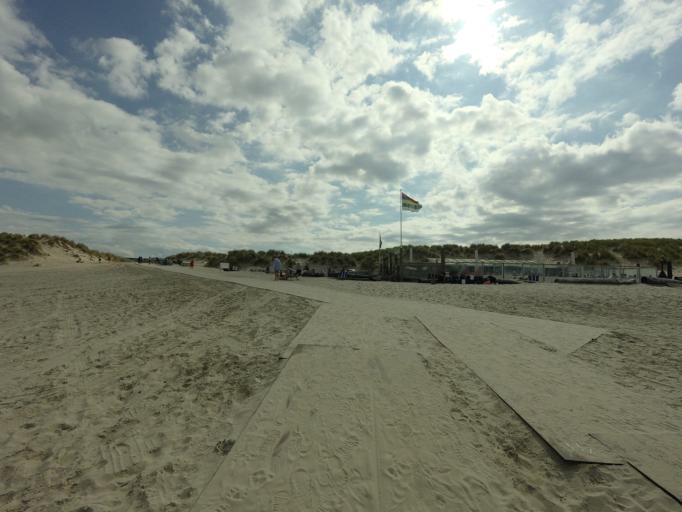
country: NL
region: Friesland
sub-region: Gemeente Terschelling
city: West-Terschelling
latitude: 53.4018
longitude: 5.2511
